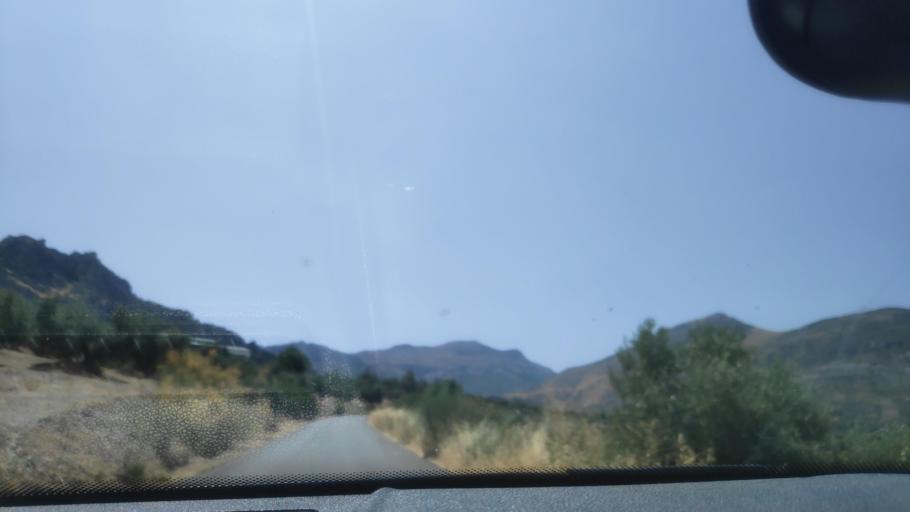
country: ES
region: Andalusia
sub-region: Provincia de Jaen
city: Jimena
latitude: 37.7946
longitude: -3.4491
